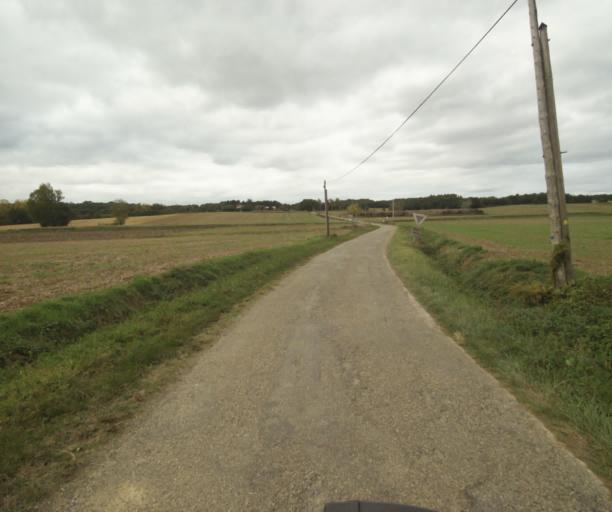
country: FR
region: Midi-Pyrenees
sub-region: Departement de la Haute-Garonne
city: Launac
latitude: 43.8394
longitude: 1.1101
